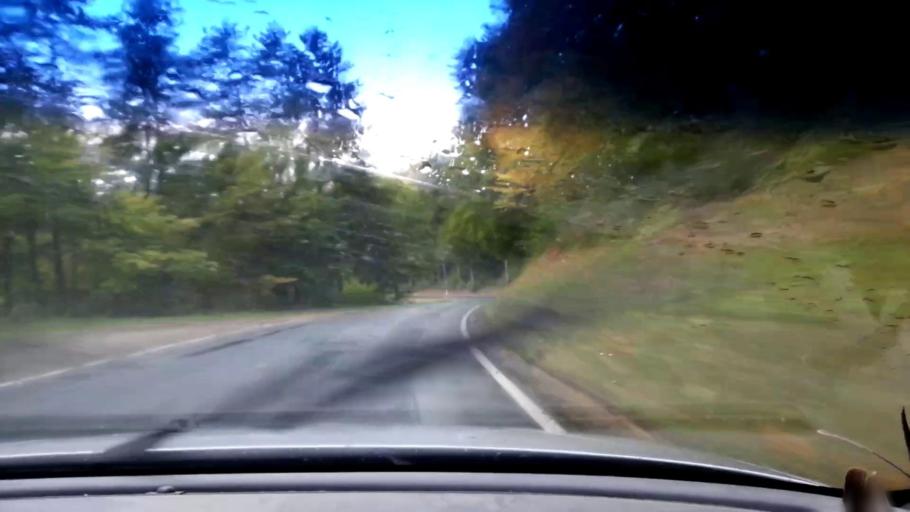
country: DE
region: Bavaria
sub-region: Upper Franconia
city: Heiligenstadt
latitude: 49.8880
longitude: 11.1622
